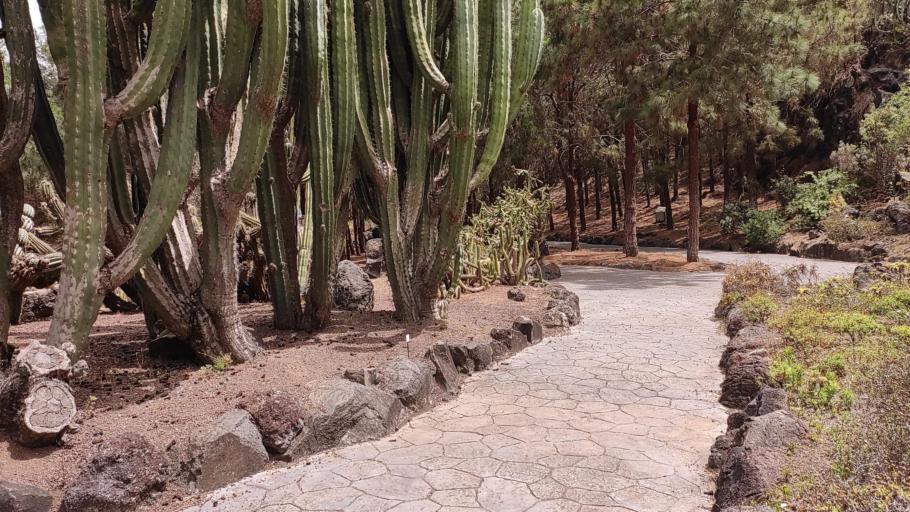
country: ES
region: Canary Islands
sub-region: Provincia de Las Palmas
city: Santa Brigida
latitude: 28.0635
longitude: -15.4622
